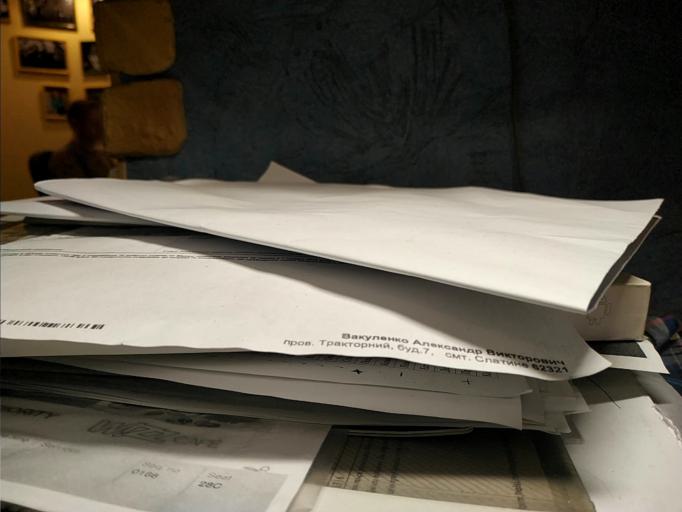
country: RU
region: Tverskaya
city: Zubtsov
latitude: 56.1130
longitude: 34.6145
